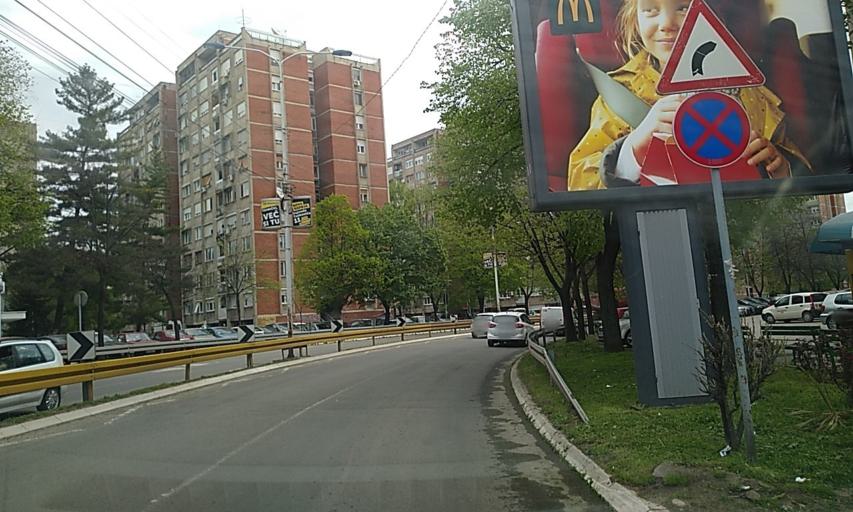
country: RS
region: Central Serbia
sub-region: Nisavski Okrug
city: Nis
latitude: 43.3249
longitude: 21.9058
